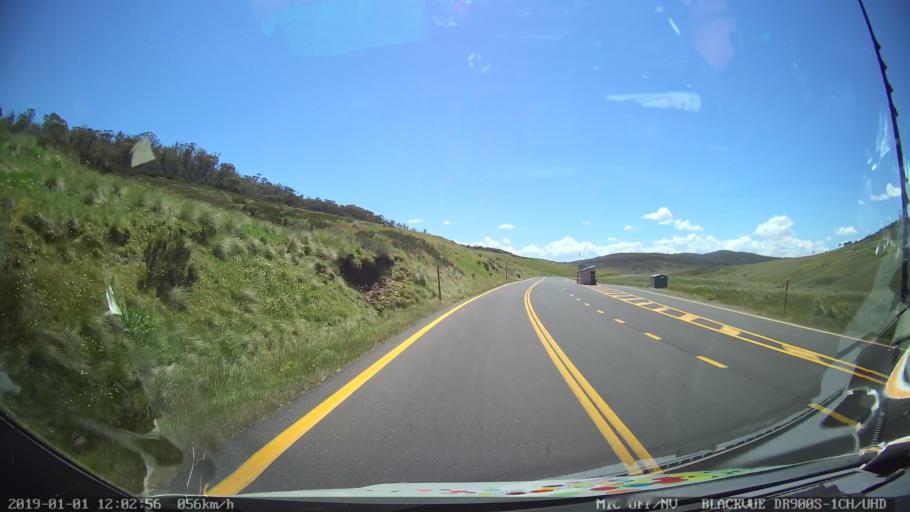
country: AU
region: New South Wales
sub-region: Snowy River
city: Jindabyne
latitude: -35.8704
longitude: 148.4817
